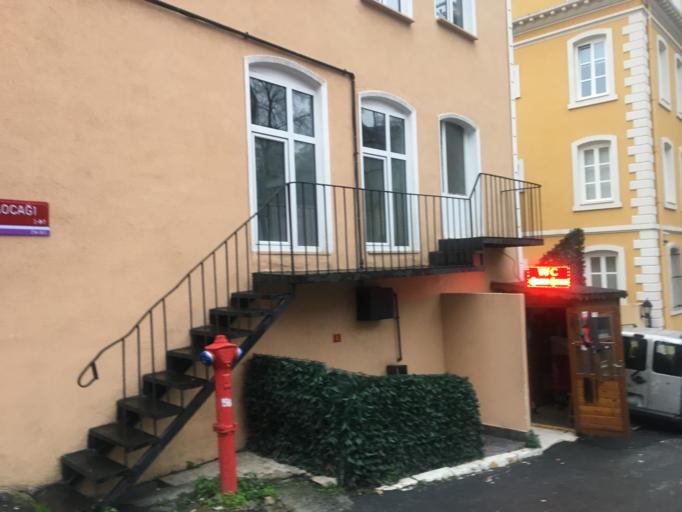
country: TR
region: Istanbul
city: Eminoenue
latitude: 41.0307
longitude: 28.9789
